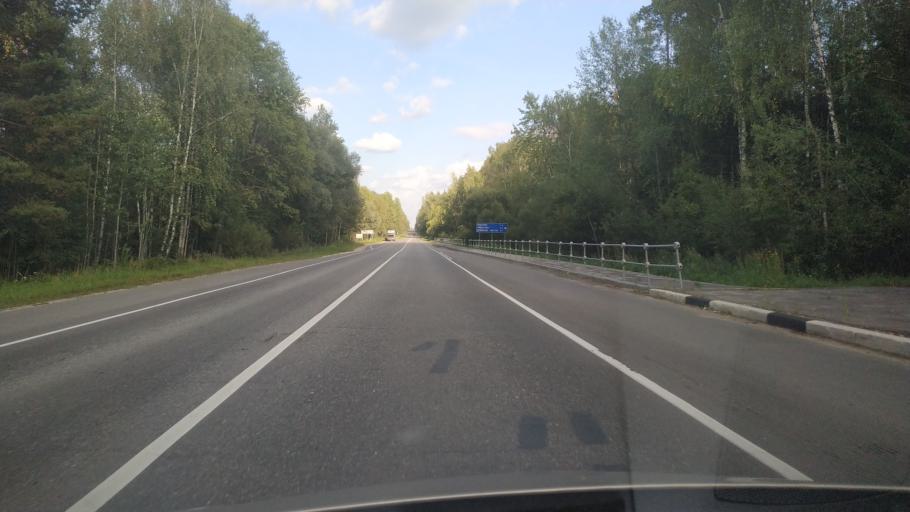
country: RU
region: Moskovskaya
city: Vereya
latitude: 55.7028
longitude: 39.1846
